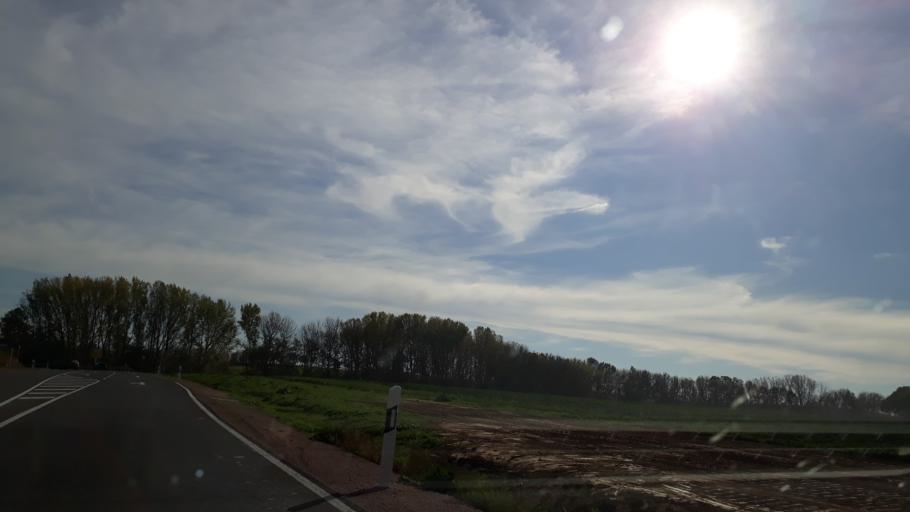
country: DE
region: Saxony
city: Mochau
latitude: 51.1123
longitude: 13.1731
